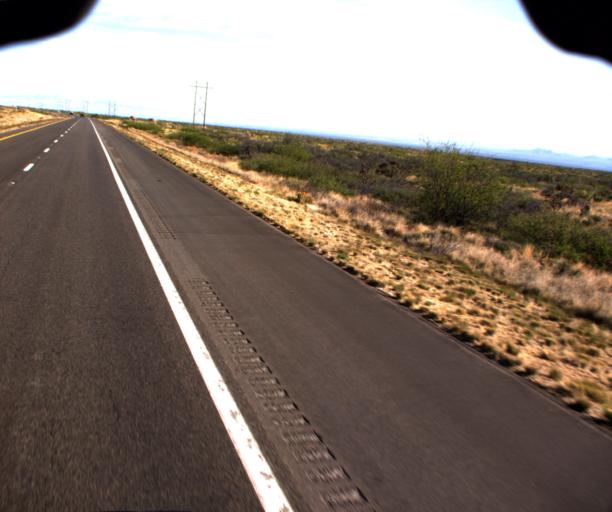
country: US
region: Arizona
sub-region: Graham County
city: Swift Trail Junction
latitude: 32.5179
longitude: -109.6737
